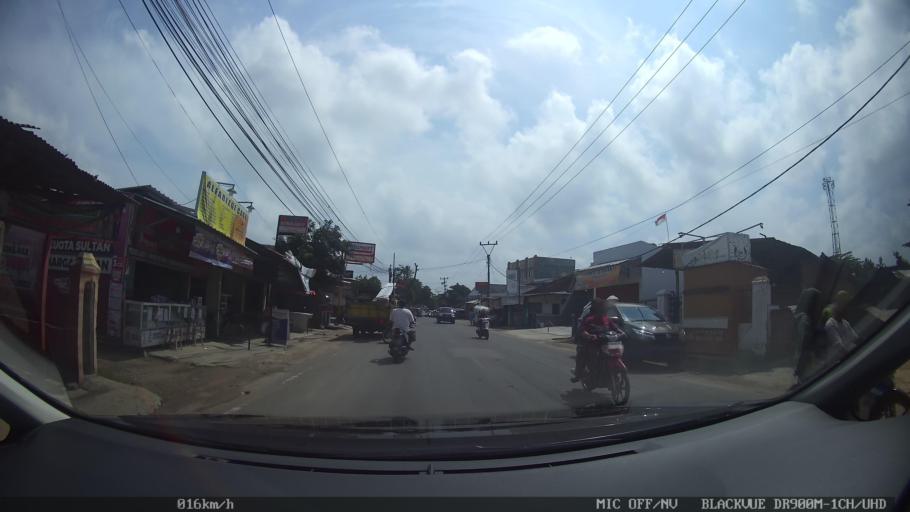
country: ID
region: Lampung
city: Kedaton
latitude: -5.3515
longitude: 105.2918
